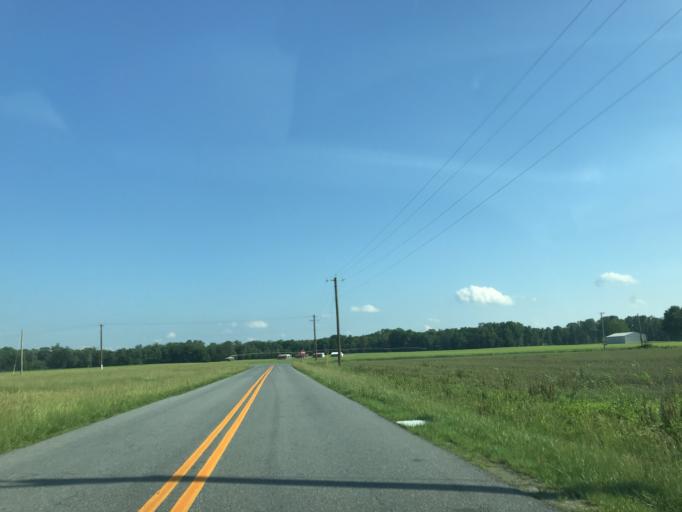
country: US
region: Maryland
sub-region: Wicomico County
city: Hebron
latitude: 38.4671
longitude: -75.6735
